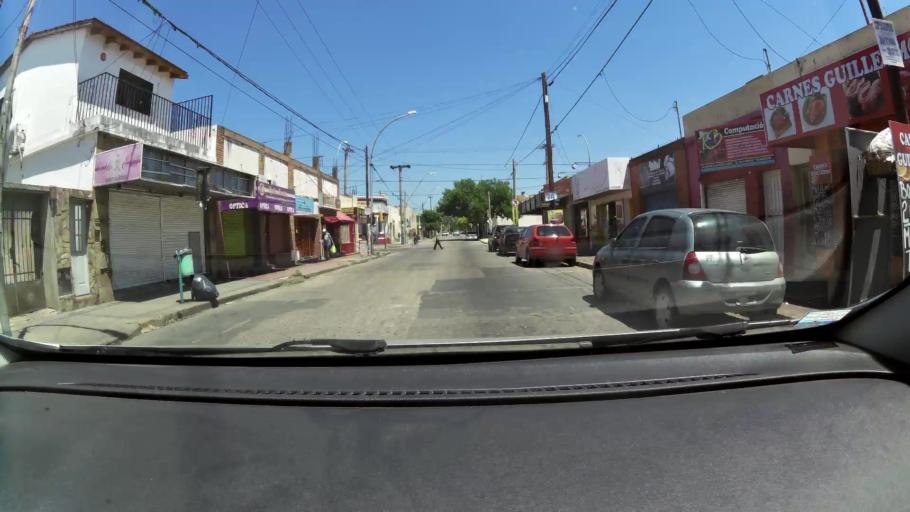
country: AR
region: Cordoba
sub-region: Departamento de Capital
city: Cordoba
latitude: -31.4136
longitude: -64.2254
